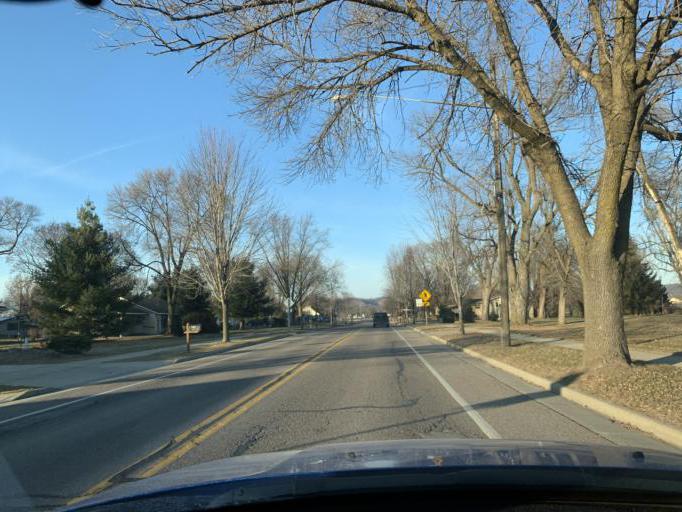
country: US
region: Wisconsin
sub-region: Sauk County
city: Spring Green
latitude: 43.1802
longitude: -90.0640
